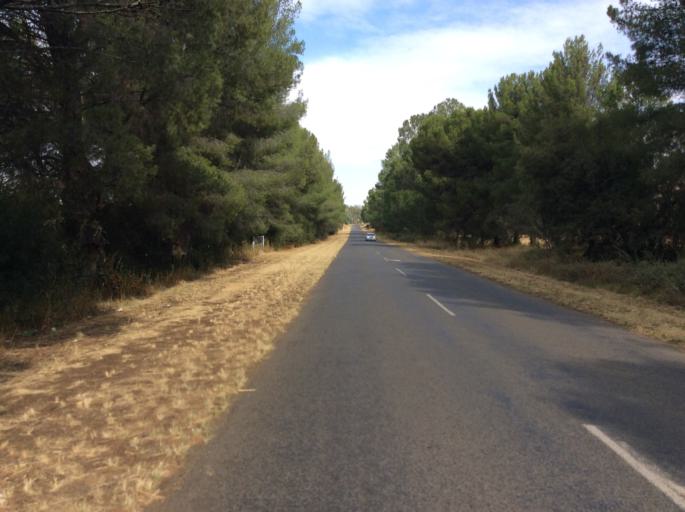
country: ZA
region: Orange Free State
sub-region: Xhariep District Municipality
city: Dewetsdorp
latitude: -29.5728
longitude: 26.6652
